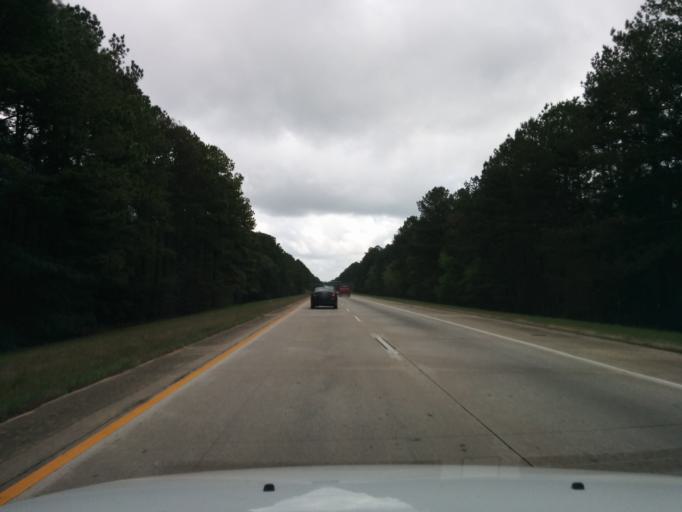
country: US
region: Georgia
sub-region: Evans County
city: Claxton
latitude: 32.2966
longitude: -81.8251
